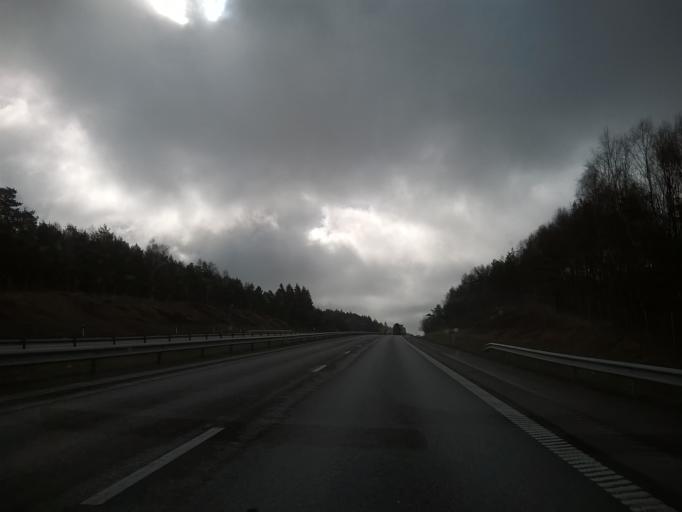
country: SE
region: Halland
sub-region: Varbergs Kommun
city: Veddige
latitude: 57.2015
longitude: 12.2481
